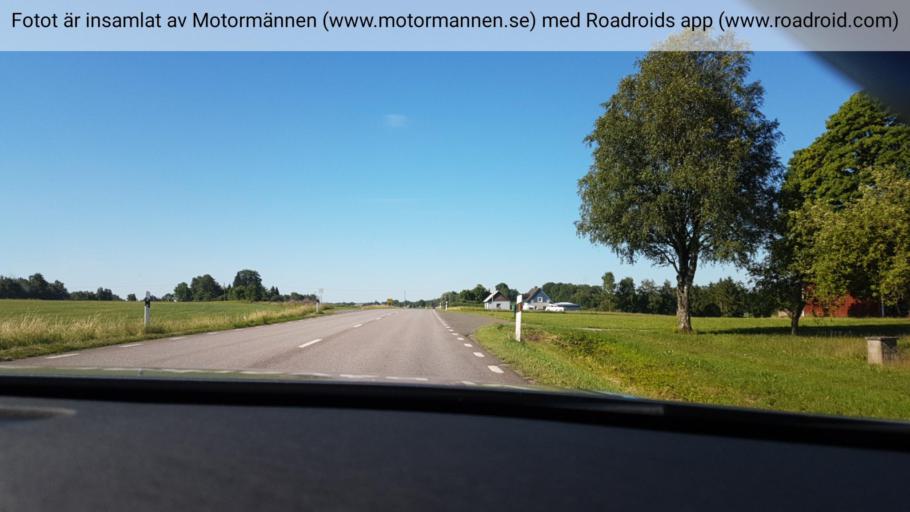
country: SE
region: Vaestra Goetaland
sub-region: Falkopings Kommun
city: Falkoeping
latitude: 58.1076
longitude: 13.5375
